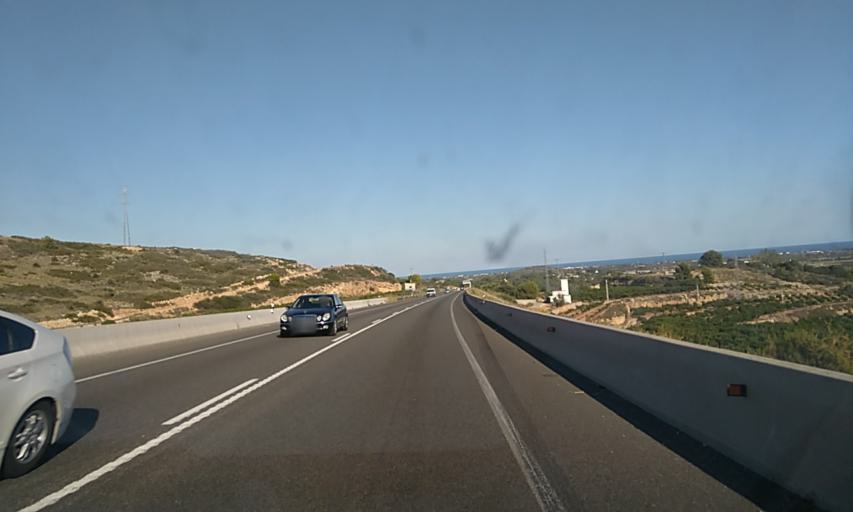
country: ES
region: Valencia
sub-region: Provincia de Castello
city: Torreblanca
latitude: 40.2307
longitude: 0.1934
